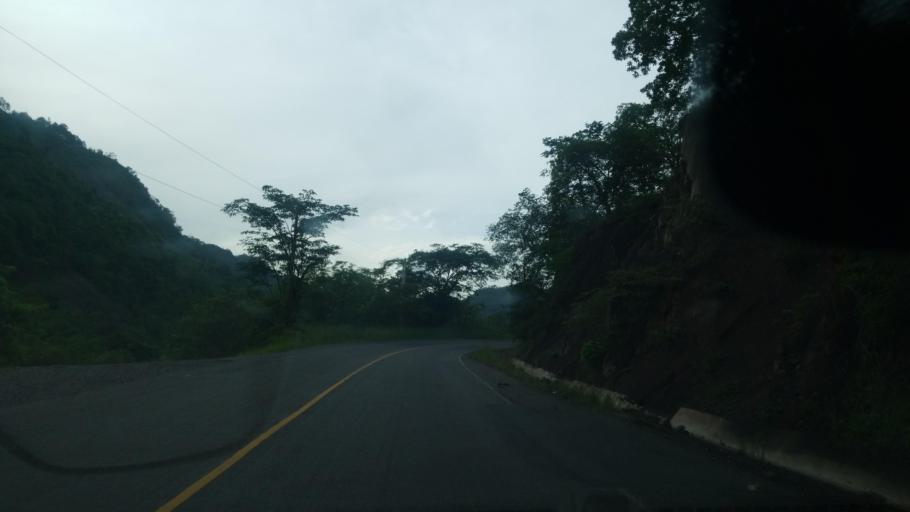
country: HN
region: Santa Barbara
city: Concepcion del Sur
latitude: 14.8147
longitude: -88.1803
